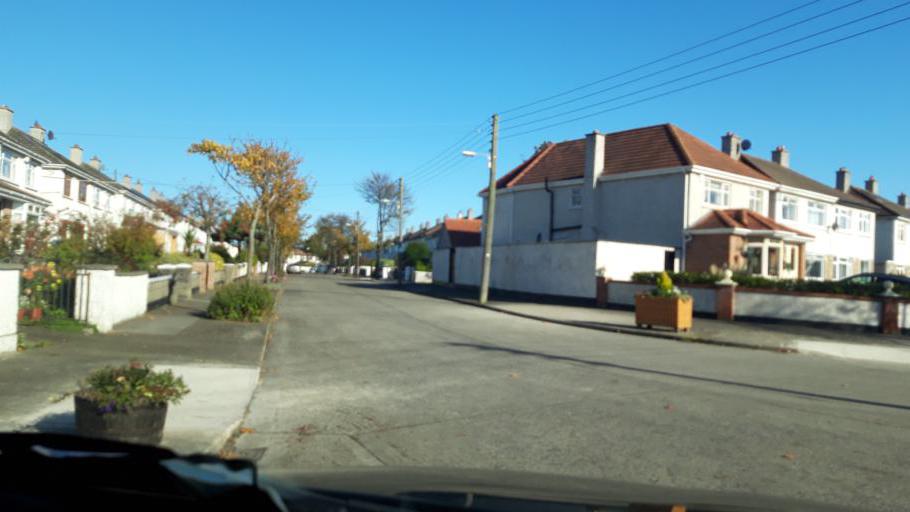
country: IE
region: Leinster
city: Raheny
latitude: 53.3875
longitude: -6.1769
